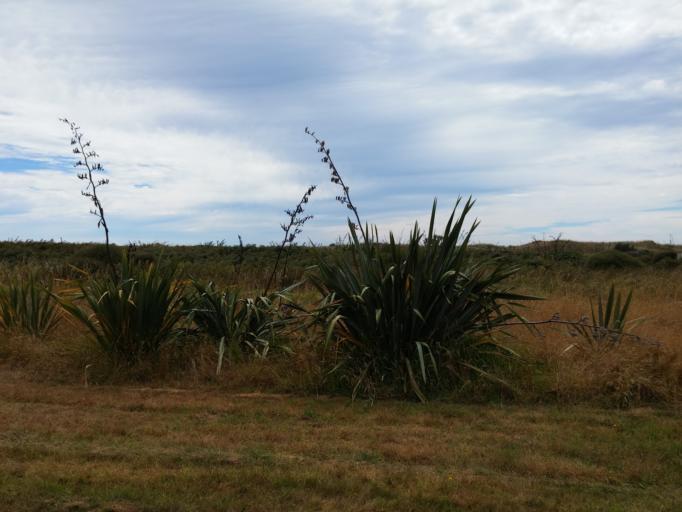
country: NZ
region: Tasman
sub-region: Tasman District
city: Takaka
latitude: -40.5452
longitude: 173.0066
